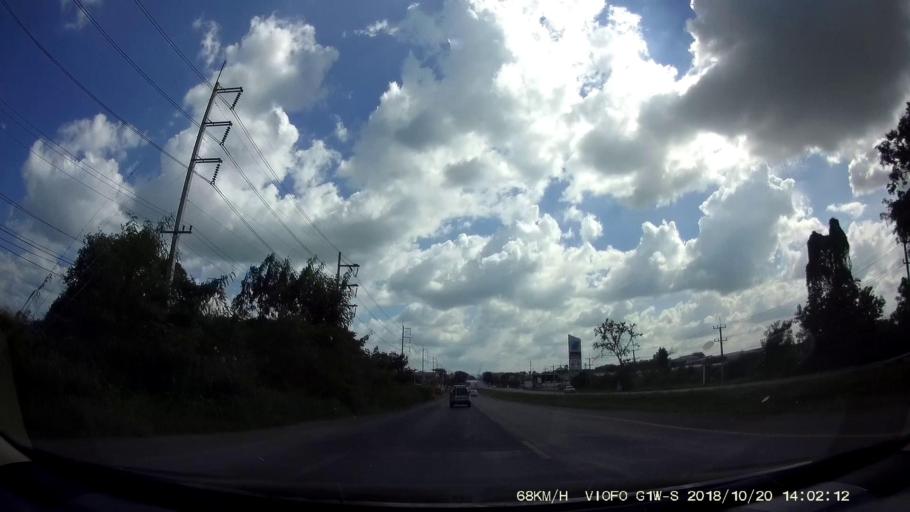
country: TH
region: Khon Kaen
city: Chum Phae
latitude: 16.4943
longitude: 102.1248
